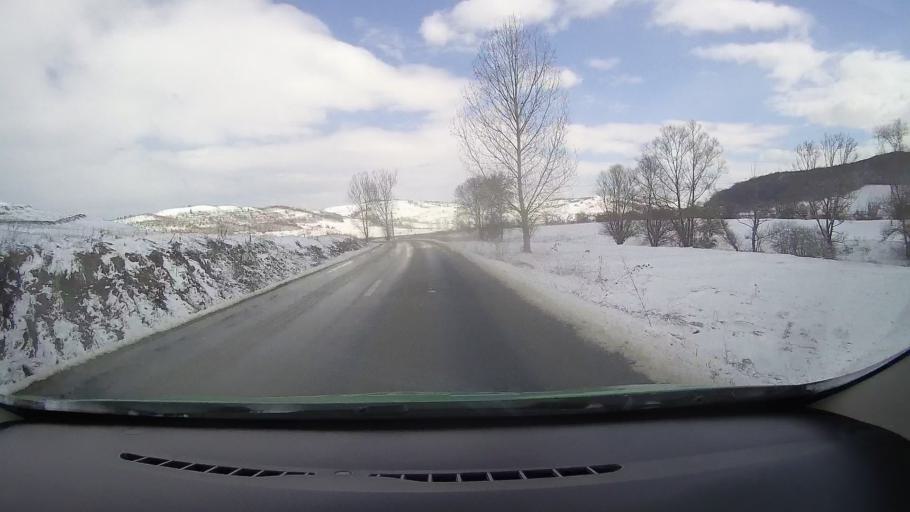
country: RO
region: Sibiu
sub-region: Comuna Altina
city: Altina
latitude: 45.9638
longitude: 24.4664
